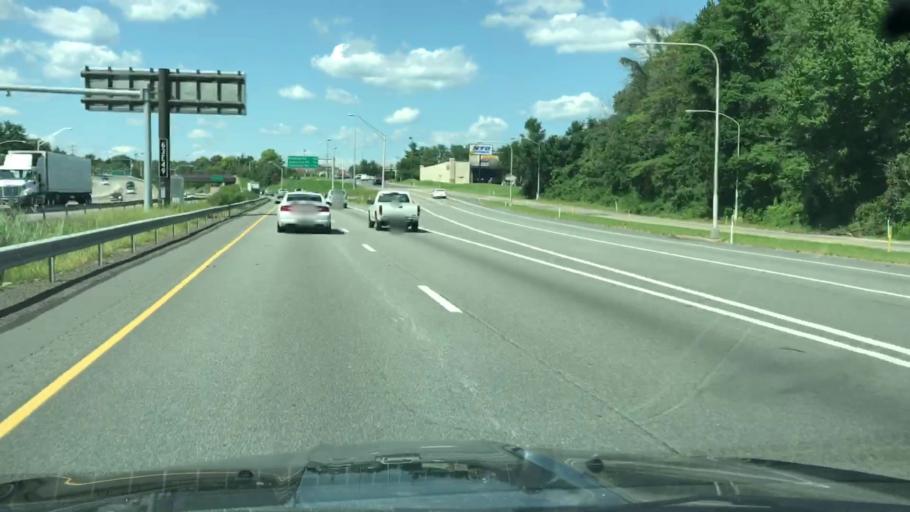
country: US
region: Pennsylvania
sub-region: Bucks County
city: Cornwells Heights
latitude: 40.0794
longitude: -74.9653
